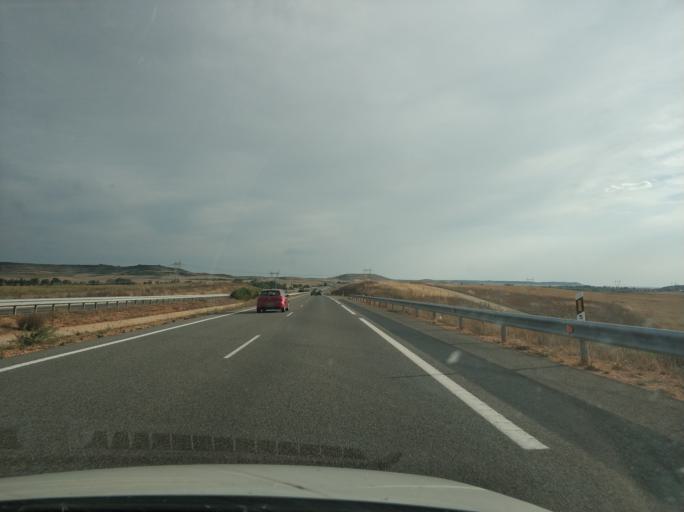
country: ES
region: Castille and Leon
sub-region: Provincia de Burgos
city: Quintanaortuno
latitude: 42.4286
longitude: -3.6949
